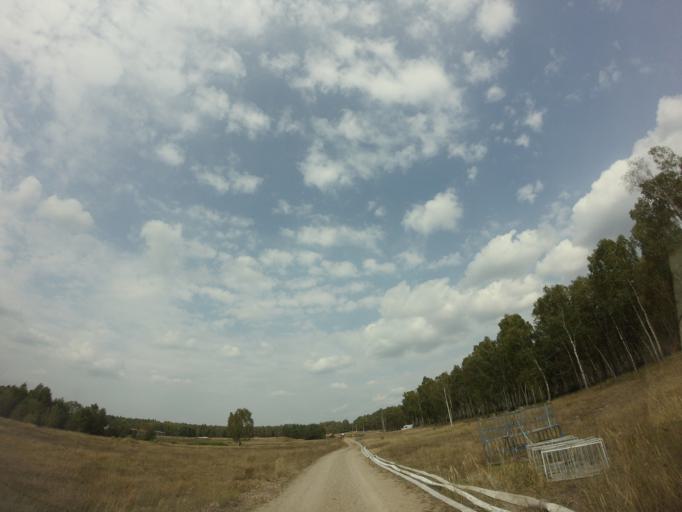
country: PL
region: West Pomeranian Voivodeship
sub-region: Powiat drawski
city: Drawsko Pomorskie
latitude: 53.4651
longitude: 15.7135
